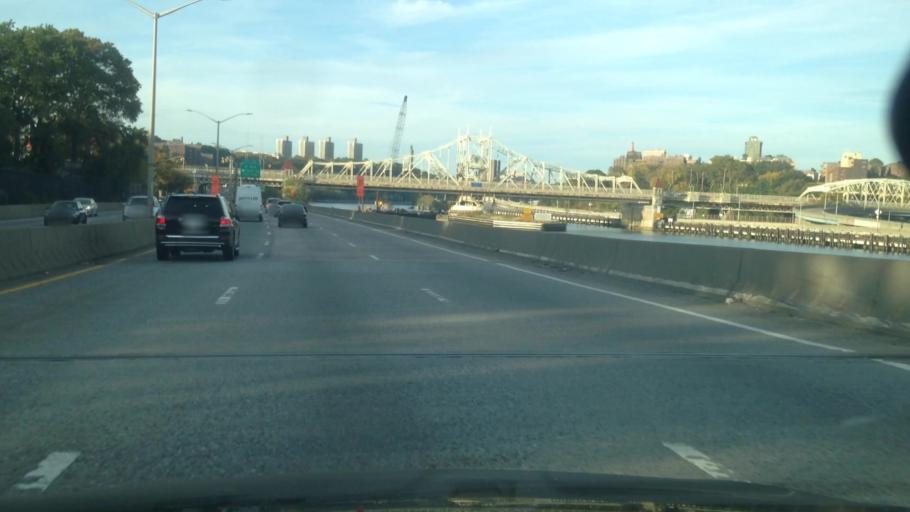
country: US
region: New York
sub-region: New York County
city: Inwood
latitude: 40.8251
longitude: -73.9344
